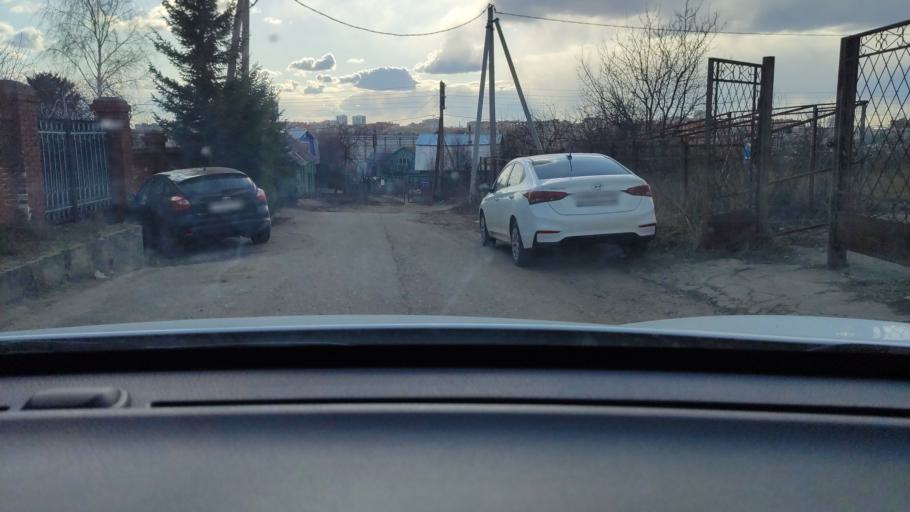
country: RU
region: Tatarstan
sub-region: Gorod Kazan'
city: Kazan
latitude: 55.8107
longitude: 49.2171
